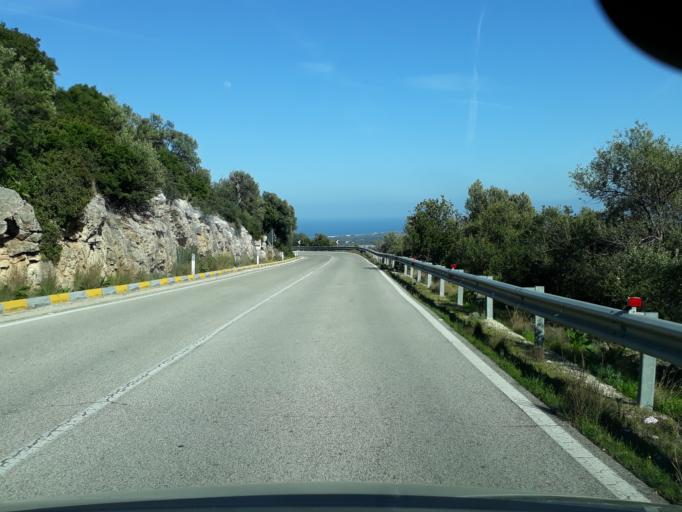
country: IT
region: Apulia
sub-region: Provincia di Bari
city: Monopoli
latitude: 40.8929
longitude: 17.2845
